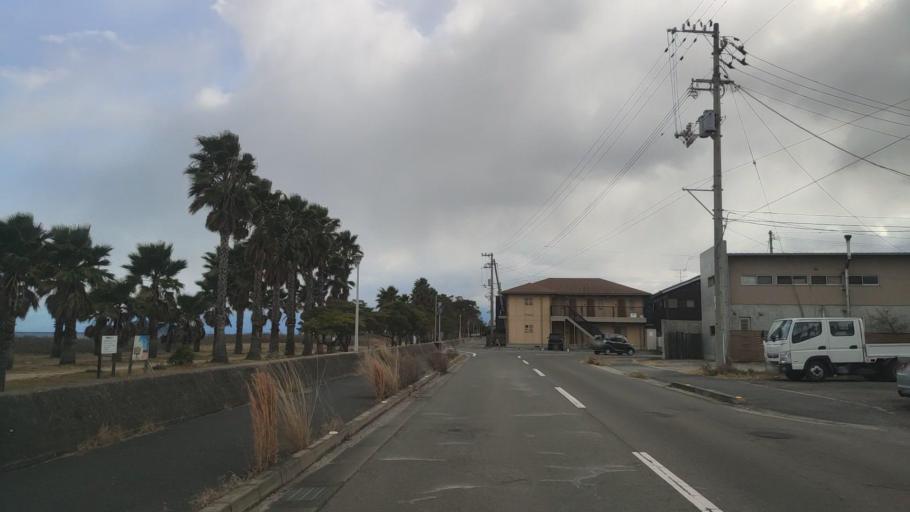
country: JP
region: Ehime
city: Saijo
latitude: 34.0452
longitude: 133.0292
